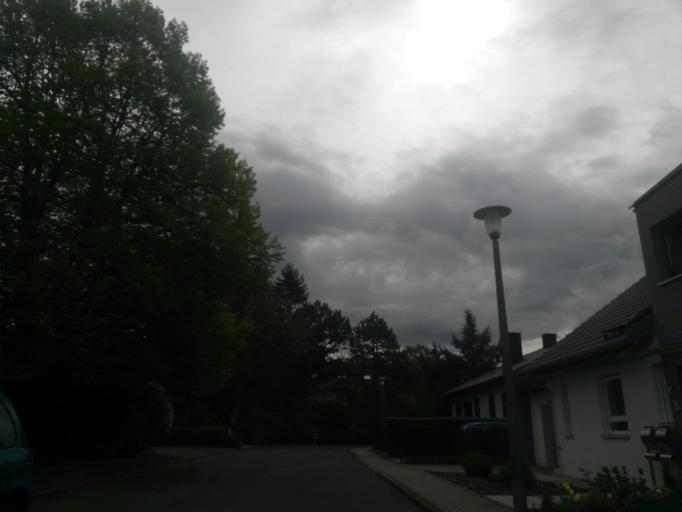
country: DE
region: Bavaria
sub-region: Regierungsbezirk Mittelfranken
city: Erlangen
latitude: 49.5504
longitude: 11.0231
